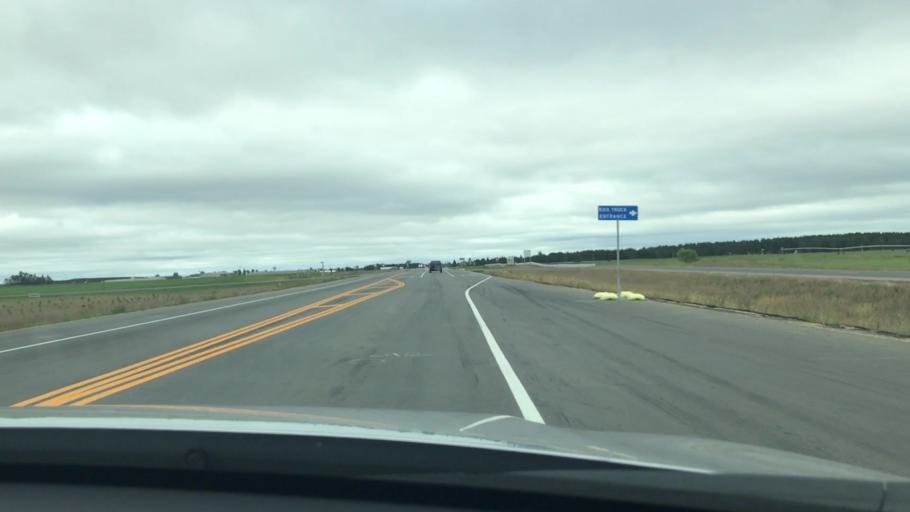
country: US
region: Minnesota
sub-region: Hubbard County
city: Park Rapids
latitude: 46.8867
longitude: -95.0631
